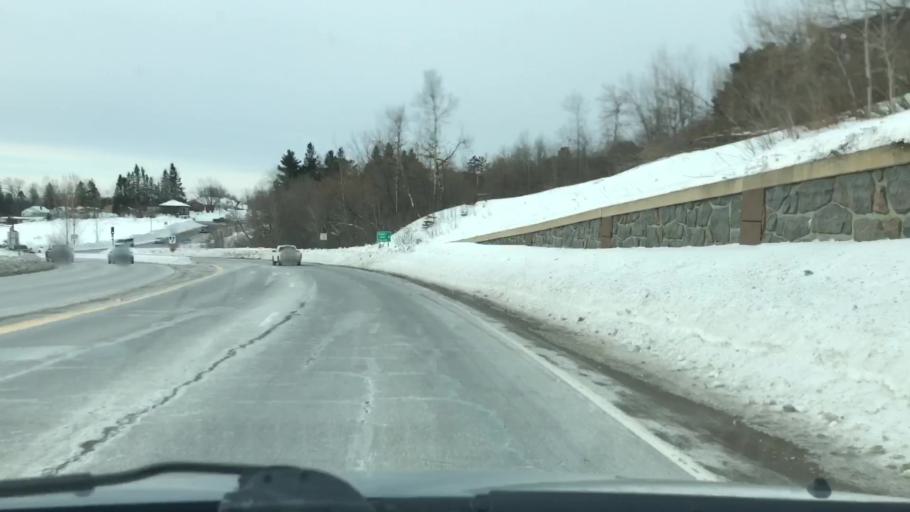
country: US
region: Minnesota
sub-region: Saint Louis County
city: Duluth
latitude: 46.7766
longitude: -92.1428
